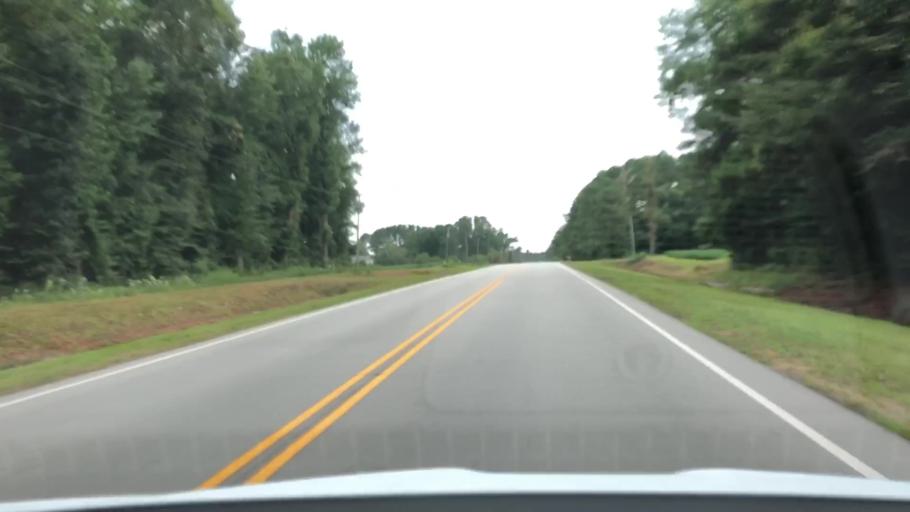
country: US
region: North Carolina
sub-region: Jones County
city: Trenton
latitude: 35.0333
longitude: -77.3205
